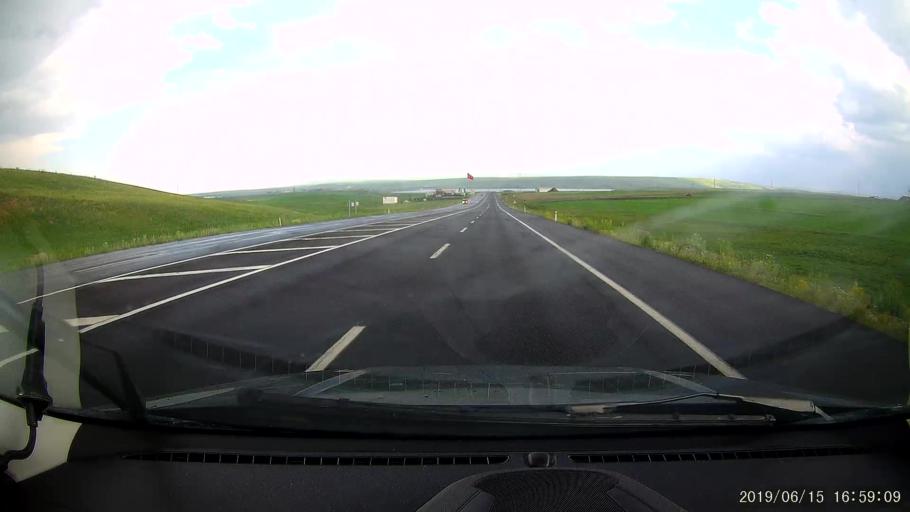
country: TR
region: Kars
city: Susuz
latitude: 40.7556
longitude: 43.1485
